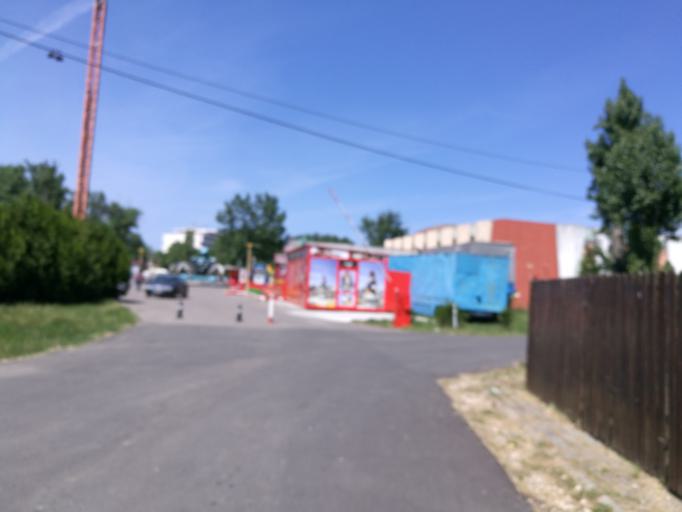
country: RO
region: Constanta
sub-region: Municipiul Constanta
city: Palazu Mare
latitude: 44.2160
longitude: 28.6311
